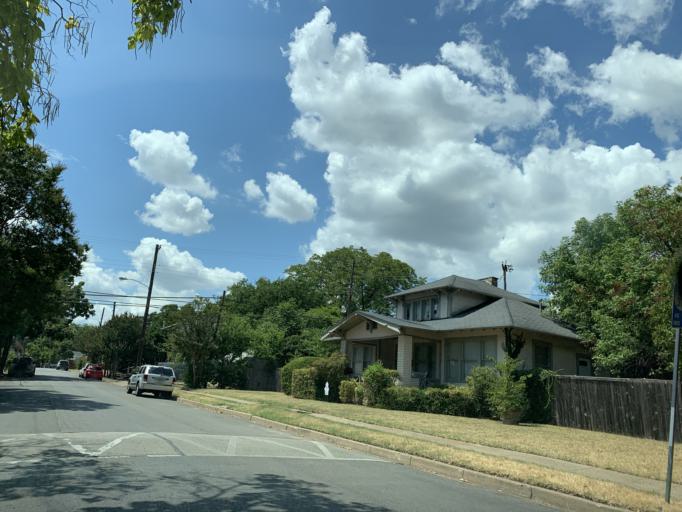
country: US
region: Texas
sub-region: Dallas County
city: Dallas
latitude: 32.7518
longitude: -96.8404
